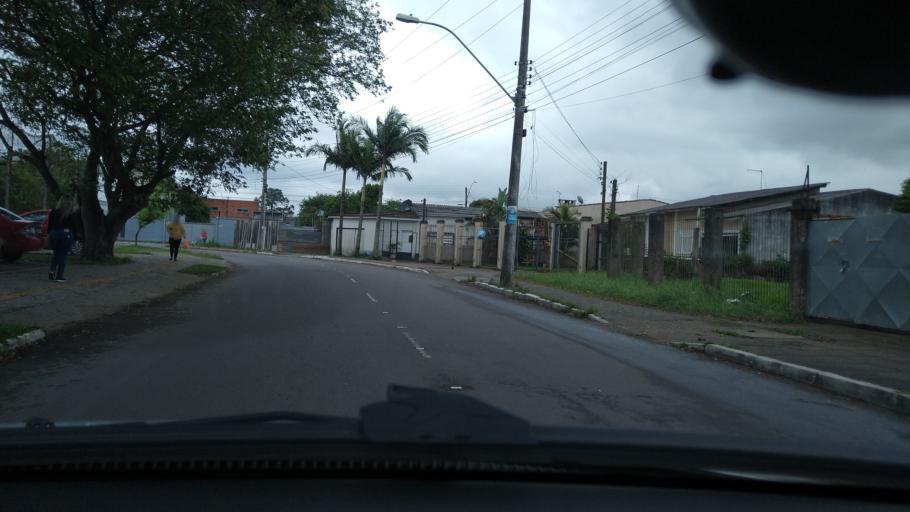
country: BR
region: Rio Grande do Sul
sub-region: Canoas
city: Canoas
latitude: -29.9007
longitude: -51.2183
